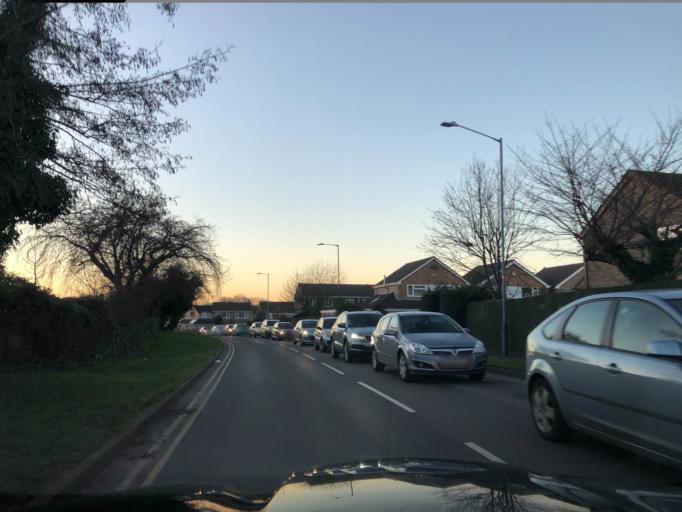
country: GB
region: England
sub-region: Warwickshire
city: Warwick
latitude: 52.2906
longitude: -1.5802
